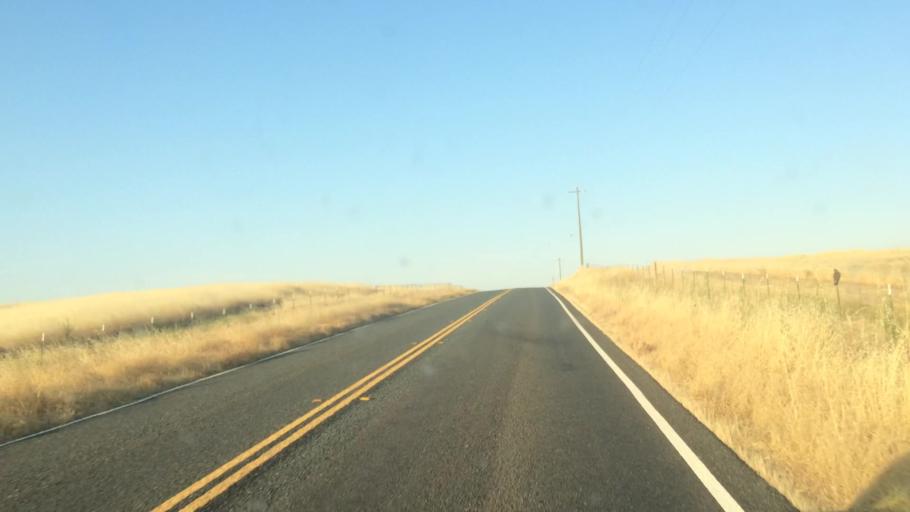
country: US
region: California
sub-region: Sacramento County
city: Clay
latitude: 38.3592
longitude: -121.0527
